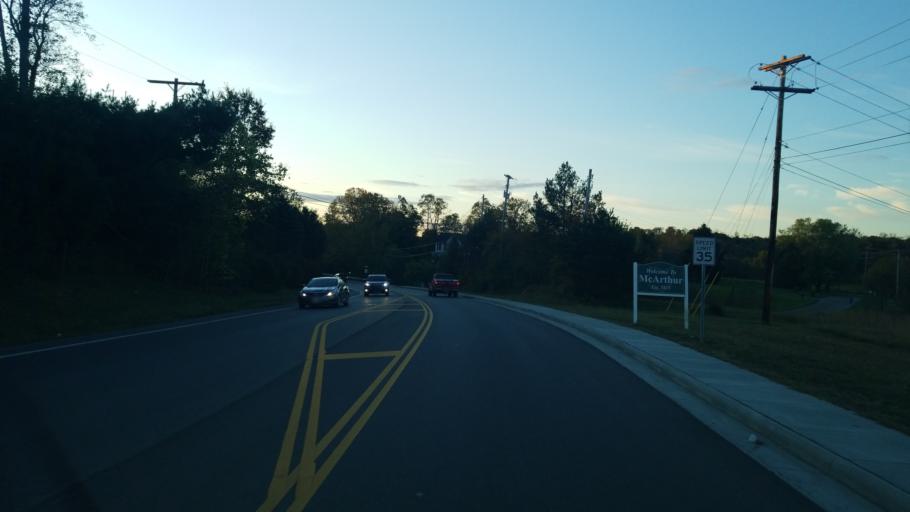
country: US
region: Ohio
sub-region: Vinton County
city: McArthur
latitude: 39.2484
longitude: -82.4880
